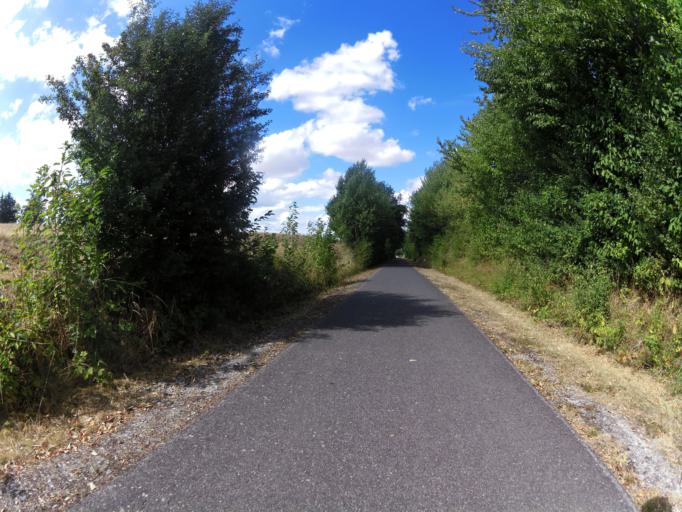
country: DE
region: Bavaria
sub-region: Regierungsbezirk Unterfranken
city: Sonderhofen
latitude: 49.5839
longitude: 10.0091
